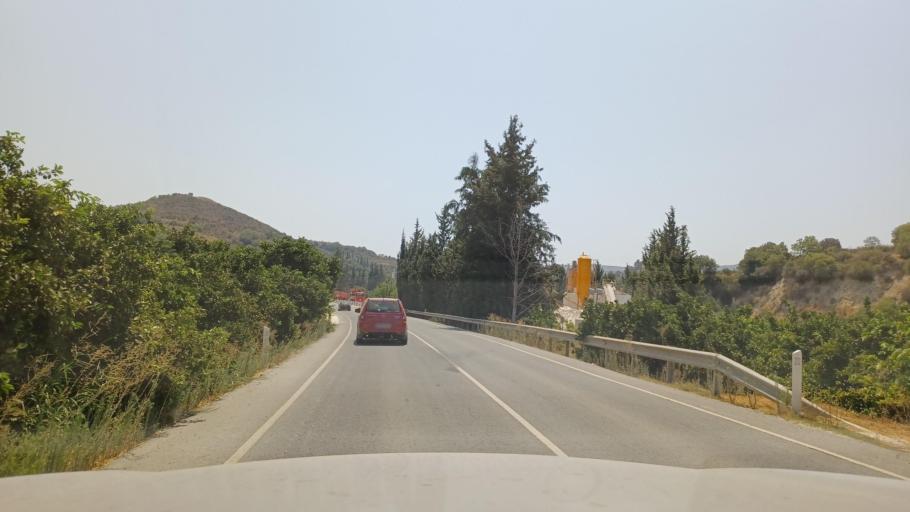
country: CY
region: Pafos
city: Polis
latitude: 34.9470
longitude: 32.4679
